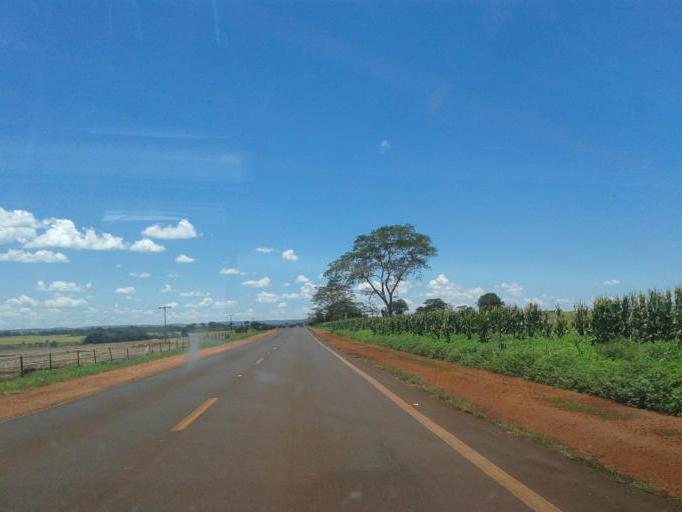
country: BR
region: Minas Gerais
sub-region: Capinopolis
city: Capinopolis
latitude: -18.6108
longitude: -49.5279
